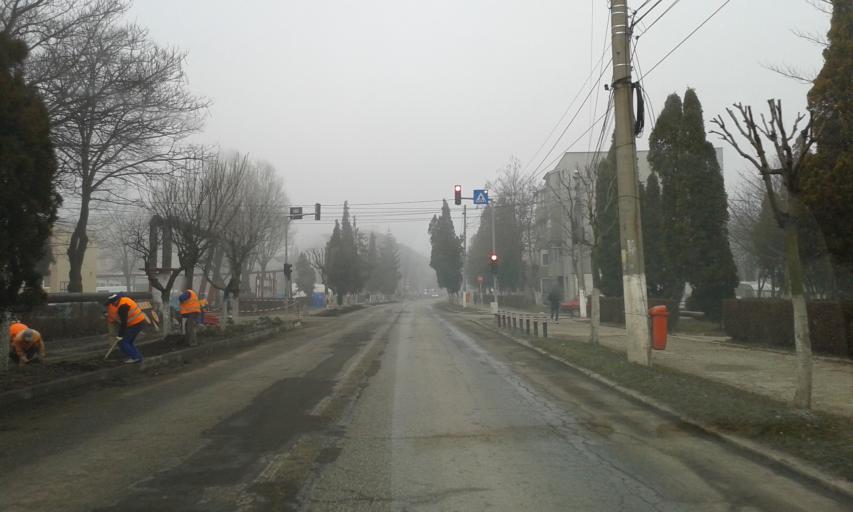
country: RO
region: Hunedoara
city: Vulcan
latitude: 45.3767
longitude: 23.2912
